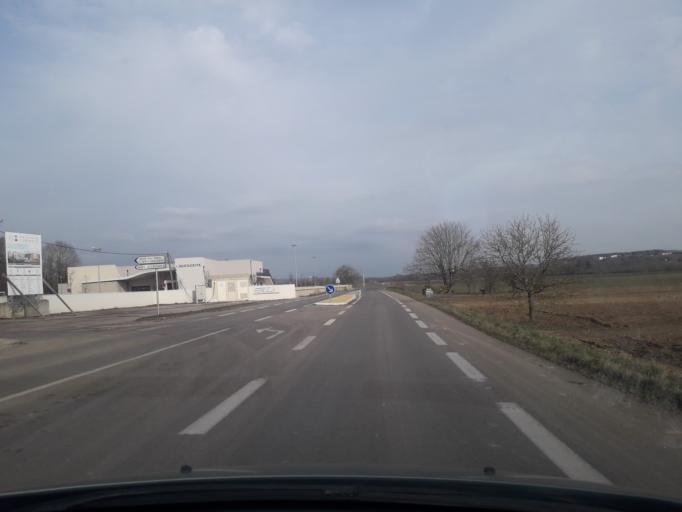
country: FR
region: Bourgogne
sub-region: Departement de la Cote-d'Or
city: Ahuy
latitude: 47.3708
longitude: 5.0253
